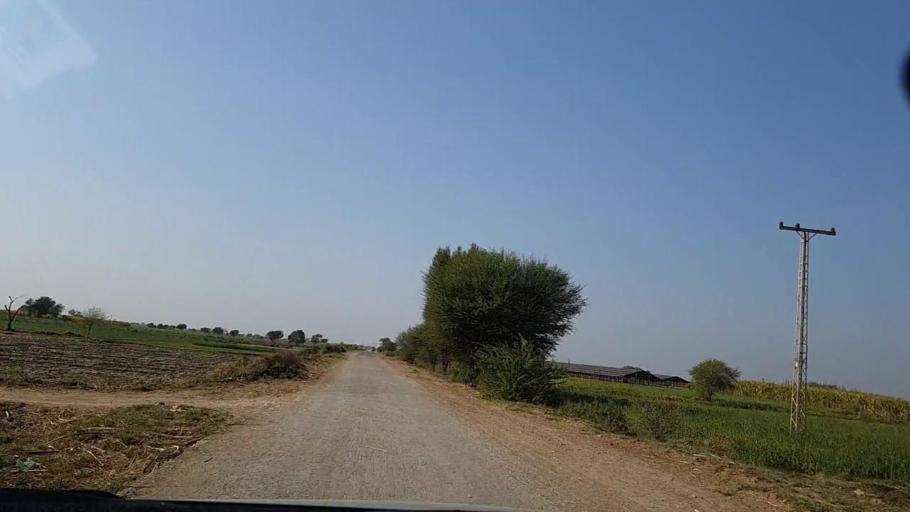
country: PK
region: Sindh
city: Digri
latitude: 25.1651
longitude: 69.0254
